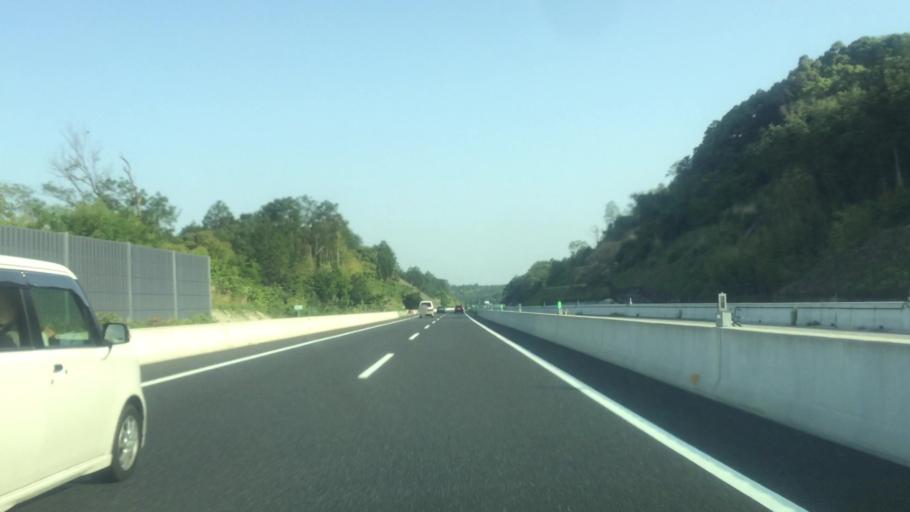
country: JP
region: Aichi
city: Okazaki
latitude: 34.9772
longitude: 137.2437
